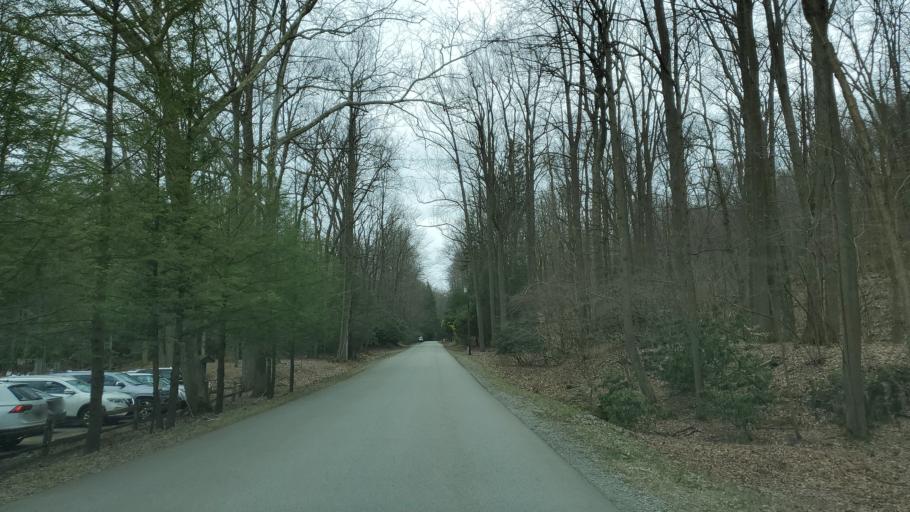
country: US
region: Pennsylvania
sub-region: Westmoreland County
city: Ligonier
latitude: 40.1689
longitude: -79.2338
